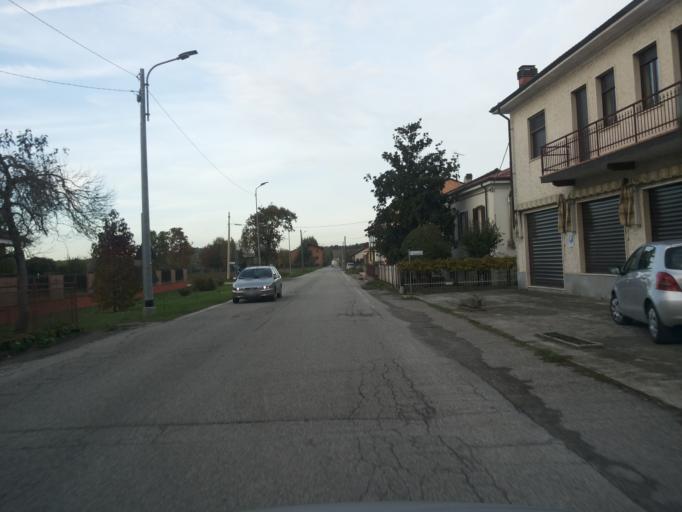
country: IT
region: Piedmont
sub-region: Provincia di Alessandria
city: Cereseto
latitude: 45.1038
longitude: 8.3073
